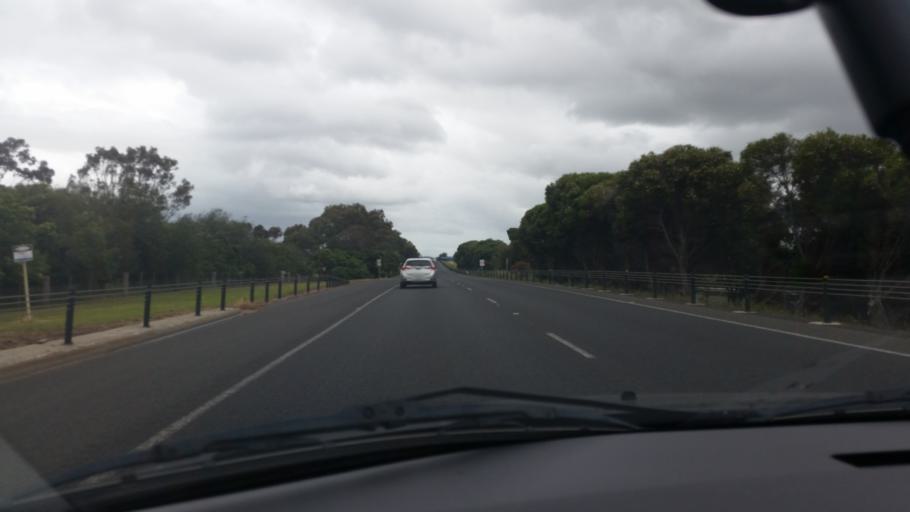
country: AU
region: Victoria
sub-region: Greater Geelong
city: Leopold
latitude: -38.1774
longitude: 144.4848
